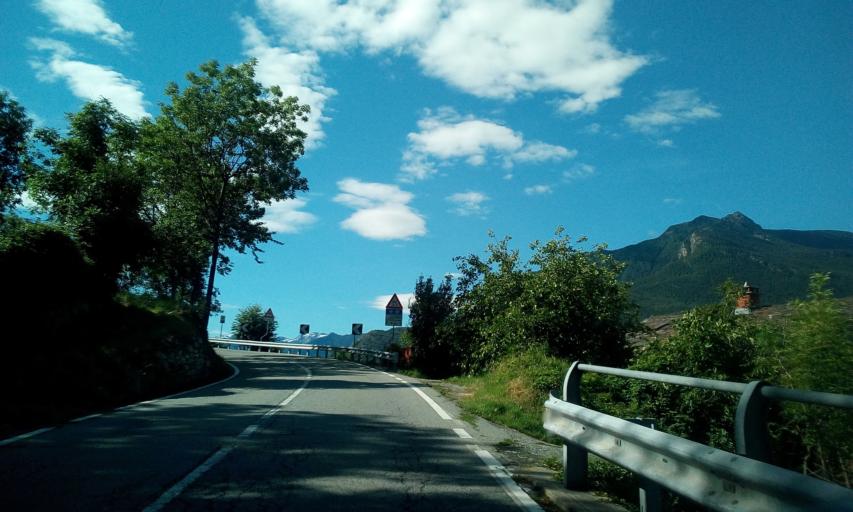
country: IT
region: Aosta Valley
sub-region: Valle d'Aosta
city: Saint-Vincent
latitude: 45.7523
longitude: 7.6559
